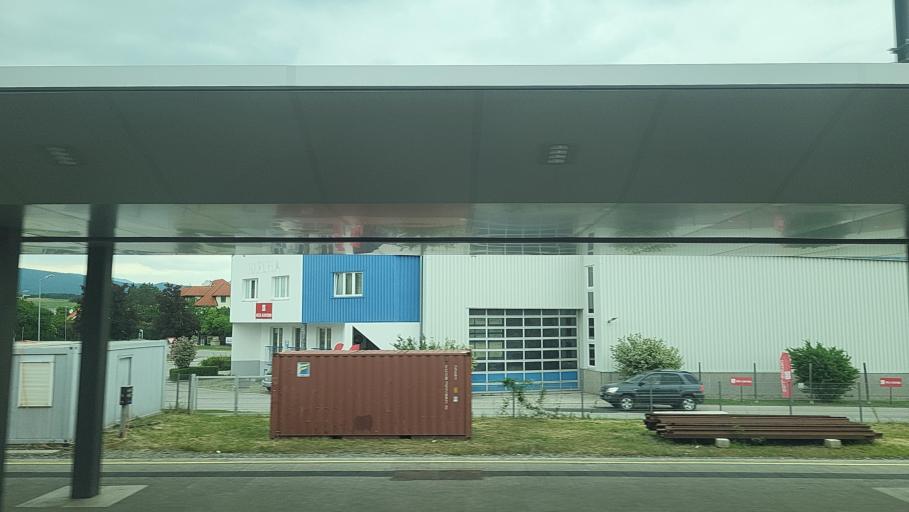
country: AT
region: Lower Austria
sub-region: Politischer Bezirk Neunkirchen
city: Neunkirchen
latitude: 47.7317
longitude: 16.0854
